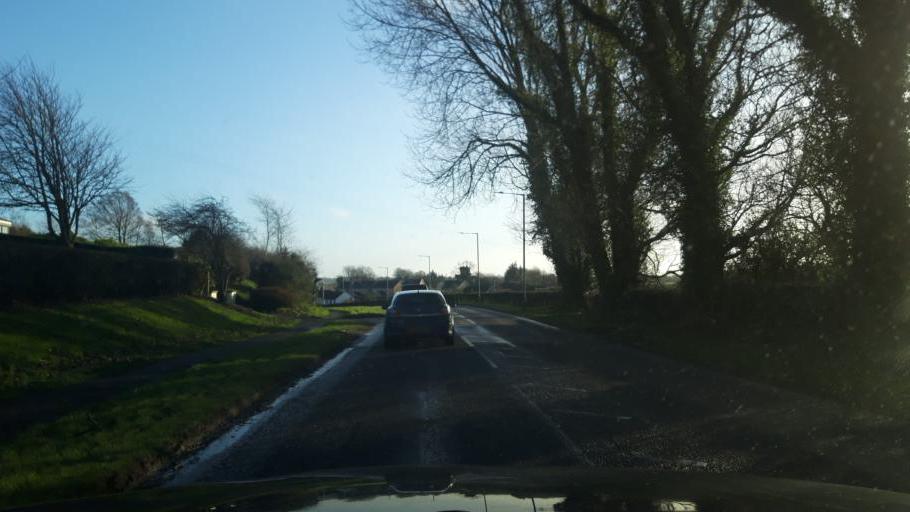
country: GB
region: Northern Ireland
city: Maghera
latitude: 54.7724
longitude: -6.6767
